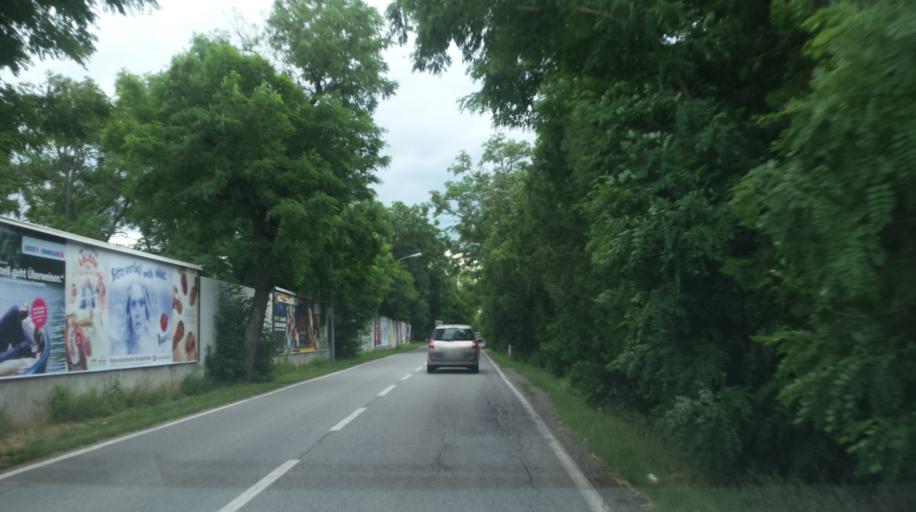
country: AT
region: Lower Austria
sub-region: Politischer Bezirk Wien-Umgebung
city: Zwolfaxing
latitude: 48.1148
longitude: 16.4588
